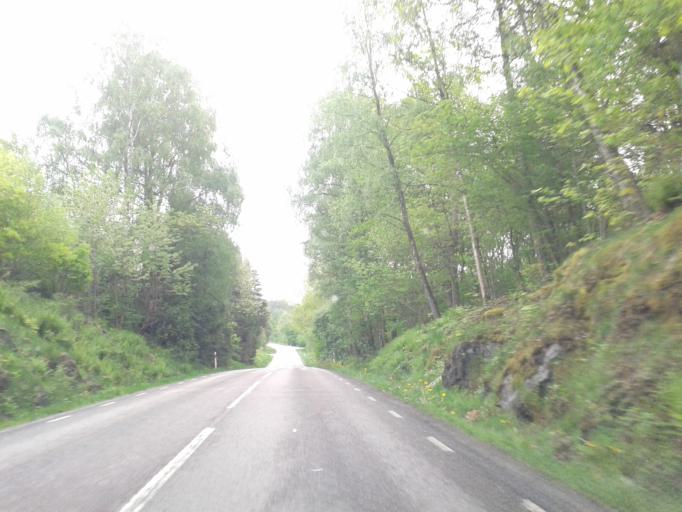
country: SE
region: Vaestra Goetaland
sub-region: Kungalvs Kommun
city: Kode
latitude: 57.8935
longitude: 11.8535
